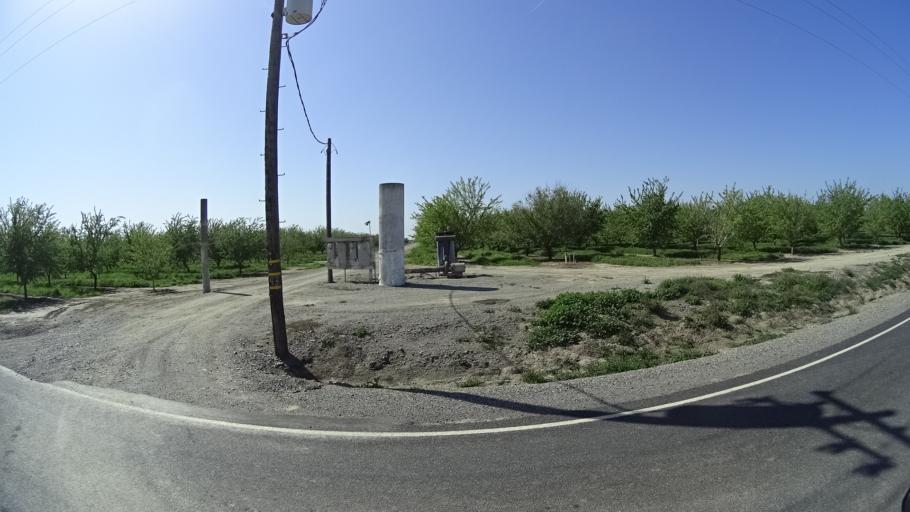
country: US
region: California
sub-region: Glenn County
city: Hamilton City
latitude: 39.6597
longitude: -122.0507
